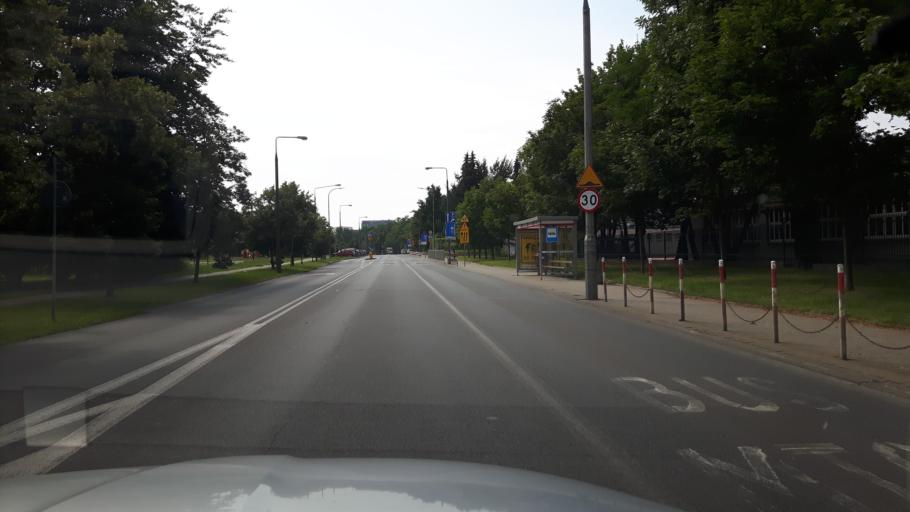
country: PL
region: Masovian Voivodeship
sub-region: Warszawa
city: Ochota
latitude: 52.2346
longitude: 20.9479
